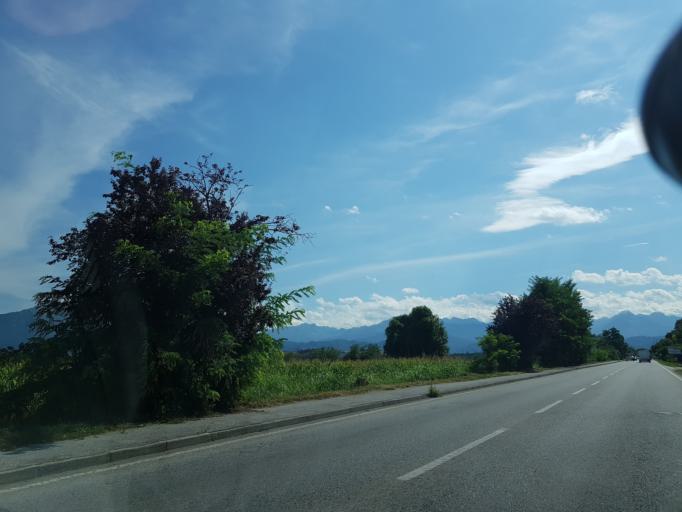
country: IT
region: Piedmont
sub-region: Provincia di Cuneo
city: Cuneo
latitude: 44.4030
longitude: 7.5443
